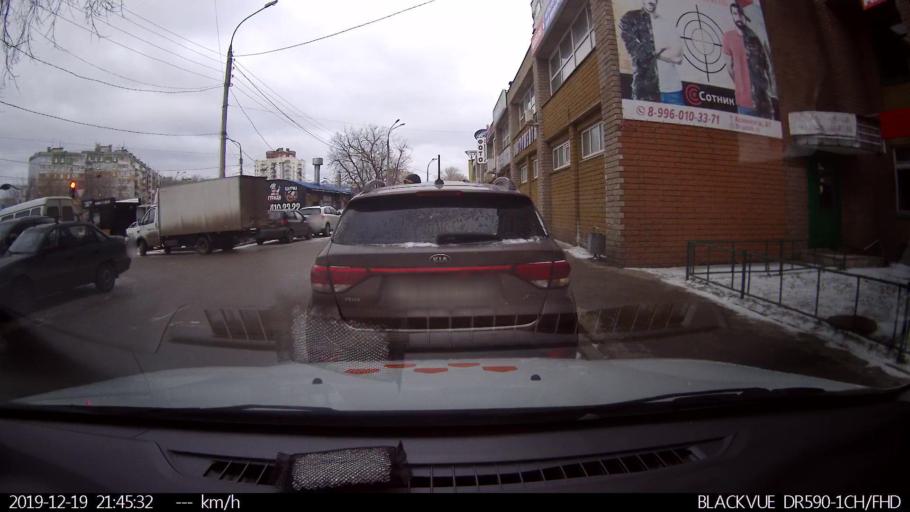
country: RU
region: Nizjnij Novgorod
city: Sitniki
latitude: 56.4293
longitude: 44.0570
